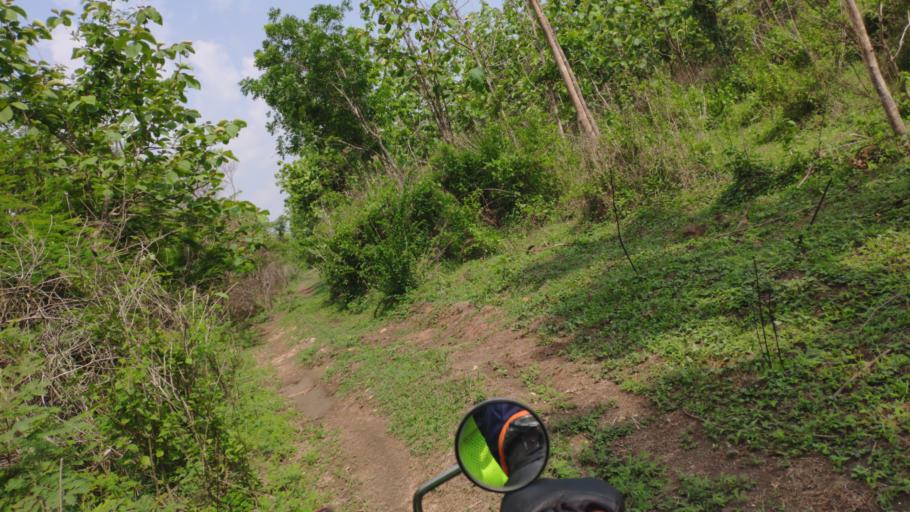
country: ID
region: Central Java
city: Temanjang
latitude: -7.1281
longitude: 111.3353
